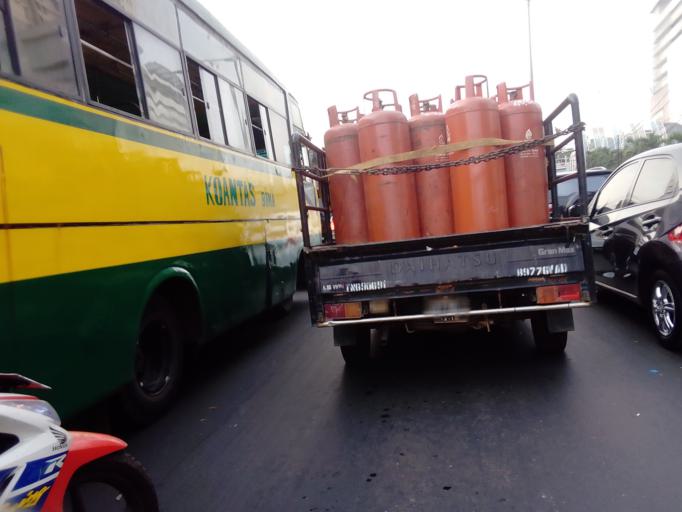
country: ID
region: Jakarta Raya
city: Jakarta
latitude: -6.1955
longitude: 106.8144
